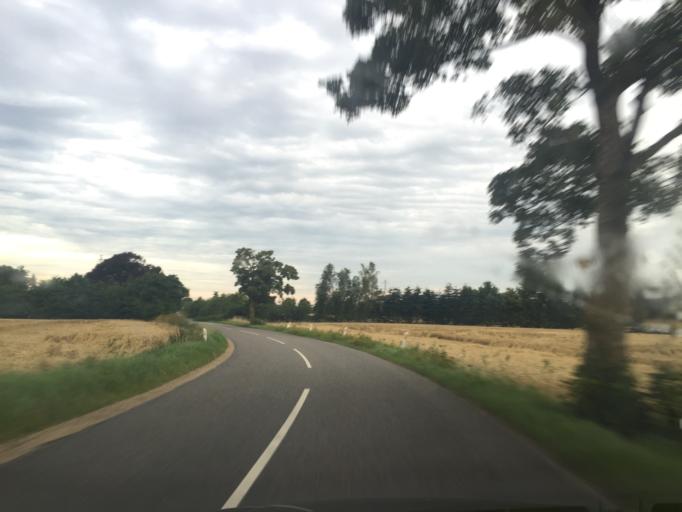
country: DK
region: Capital Region
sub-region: Egedal Kommune
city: Vekso
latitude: 55.7040
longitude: 12.2297
